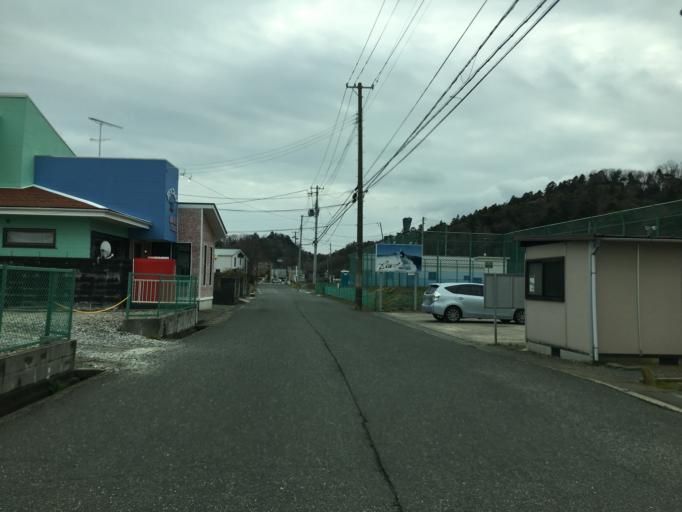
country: JP
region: Fukushima
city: Iwaki
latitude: 36.9465
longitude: 140.9243
